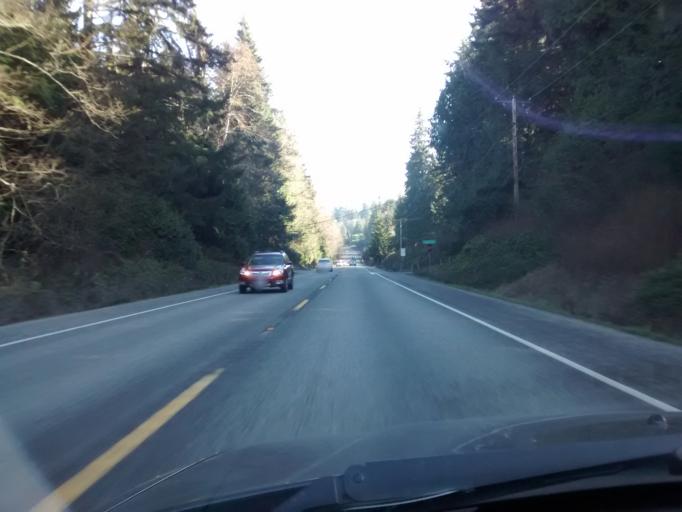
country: US
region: Washington
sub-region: Kitsap County
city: Lofall
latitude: 47.8303
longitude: -122.6280
